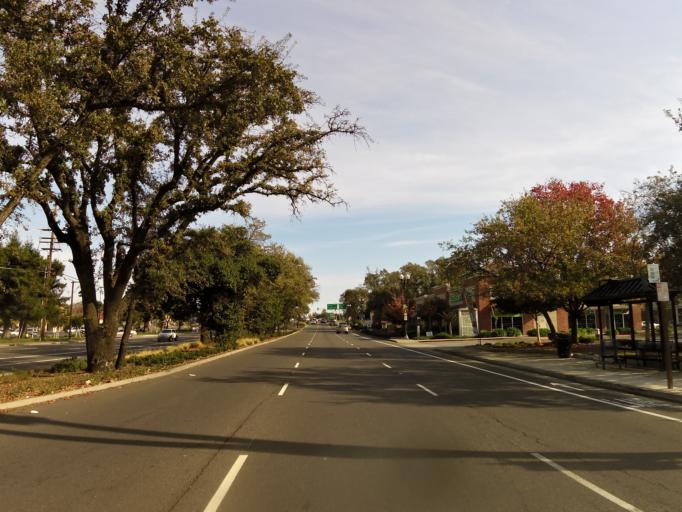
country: US
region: California
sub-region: Sacramento County
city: Elk Grove
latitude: 38.4090
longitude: -121.3925
